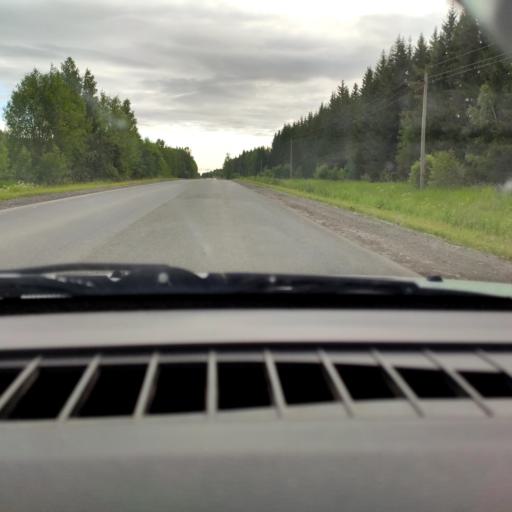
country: RU
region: Perm
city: Orda
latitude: 57.2314
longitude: 56.9693
